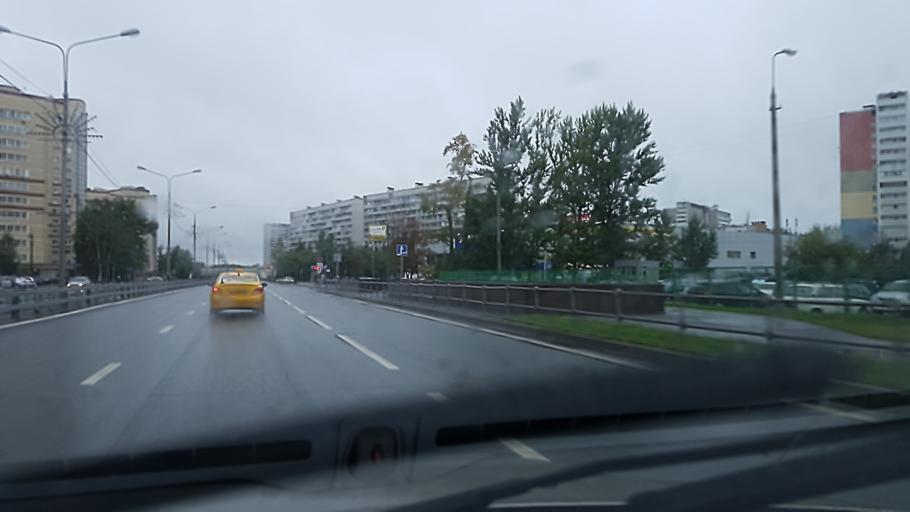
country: RU
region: Moscow
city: Zelenograd
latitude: 55.9801
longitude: 37.1857
